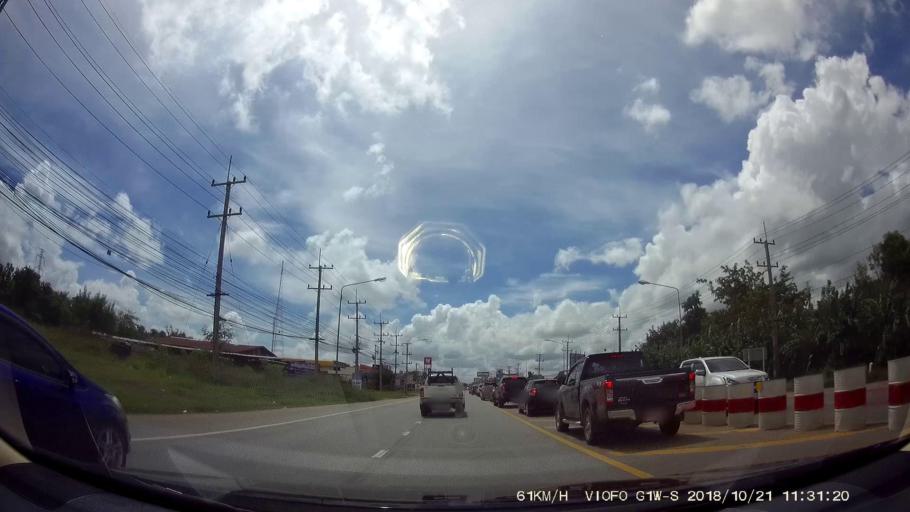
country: TH
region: Chaiyaphum
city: Chaiyaphum
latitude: 15.7700
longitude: 102.0256
